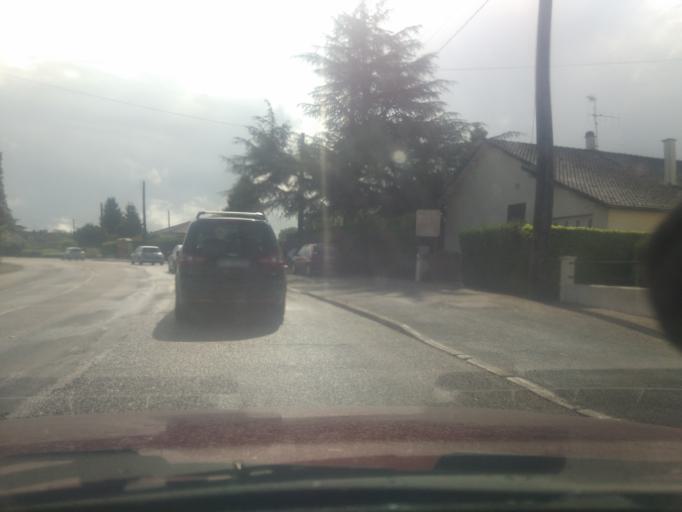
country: FR
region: Poitou-Charentes
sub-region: Departement des Deux-Sevres
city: Parthenay
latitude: 46.6340
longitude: -0.2508
